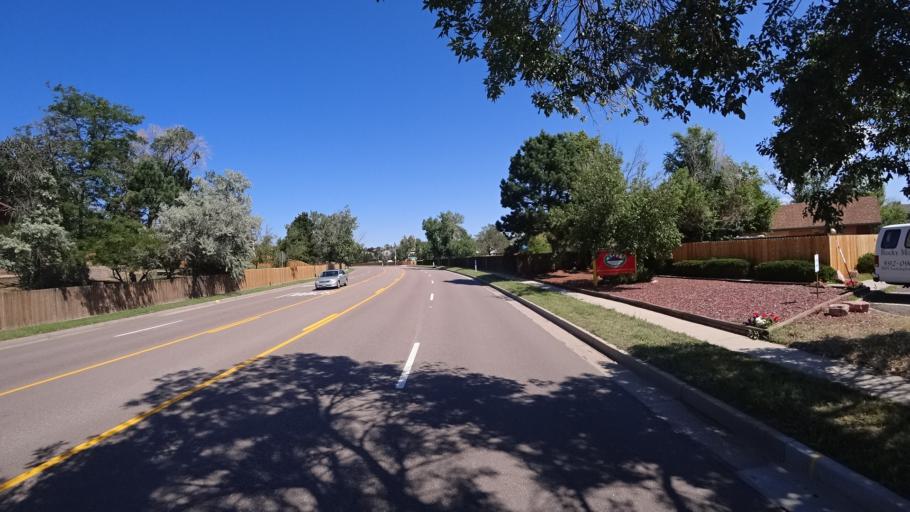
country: US
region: Colorado
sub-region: El Paso County
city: Black Forest
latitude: 38.9423
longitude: -104.7631
